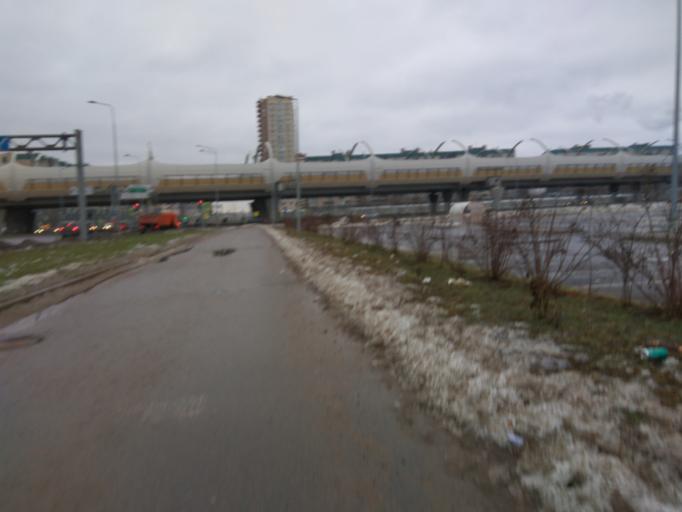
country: RU
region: St.-Petersburg
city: Staraya Derevnya
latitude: 60.0039
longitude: 30.2305
